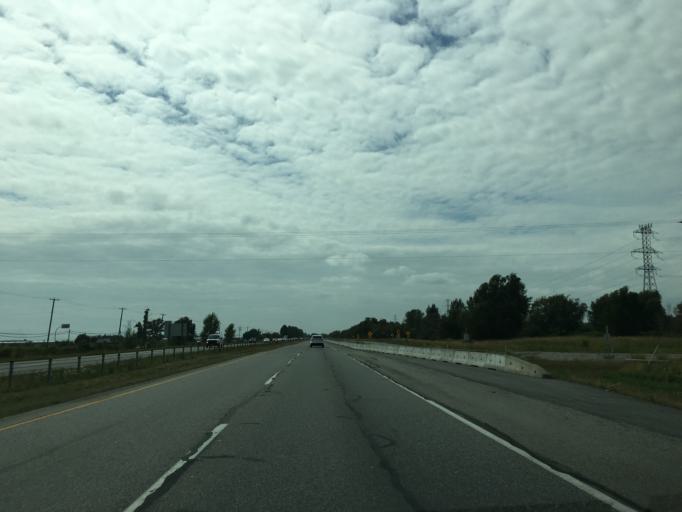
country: CA
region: British Columbia
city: Delta
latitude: 49.0905
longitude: -122.9784
